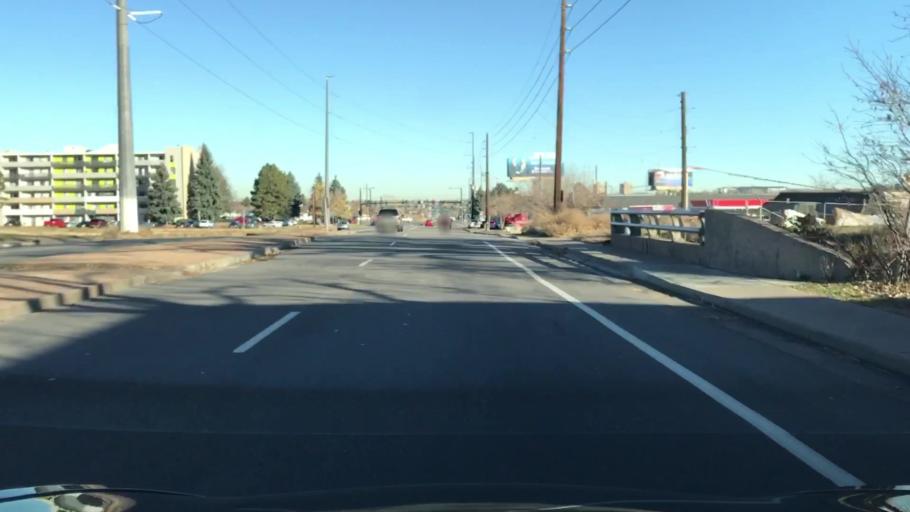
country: US
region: Colorado
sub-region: Arapahoe County
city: Glendale
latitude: 39.6744
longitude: -104.9035
